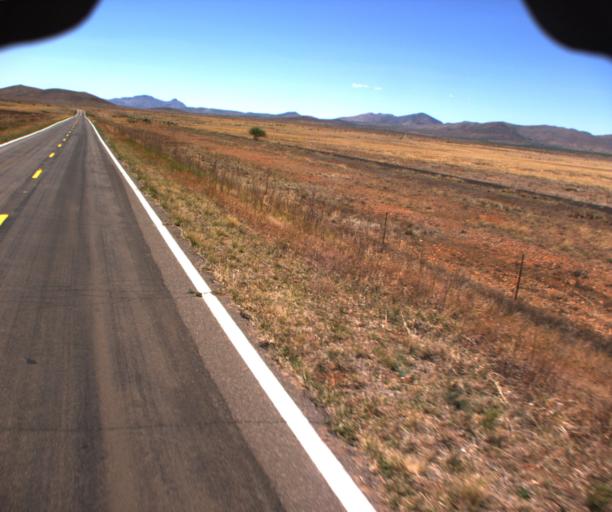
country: US
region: Arizona
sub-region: Cochise County
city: Douglas
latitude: 31.5864
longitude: -109.2478
